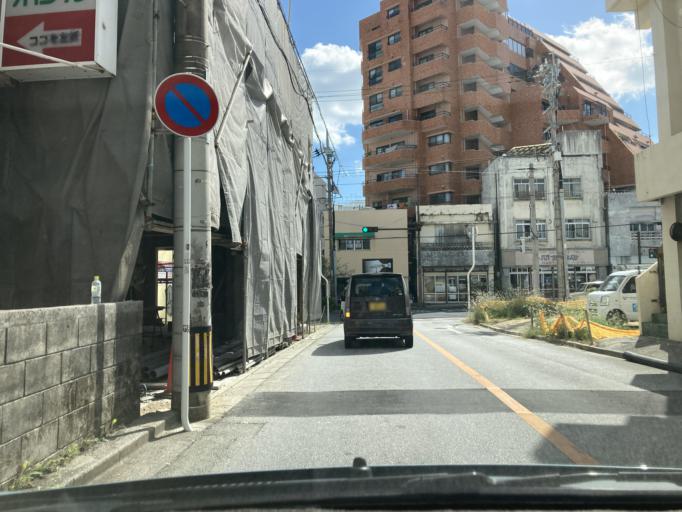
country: JP
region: Okinawa
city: Okinawa
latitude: 26.3378
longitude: 127.8020
